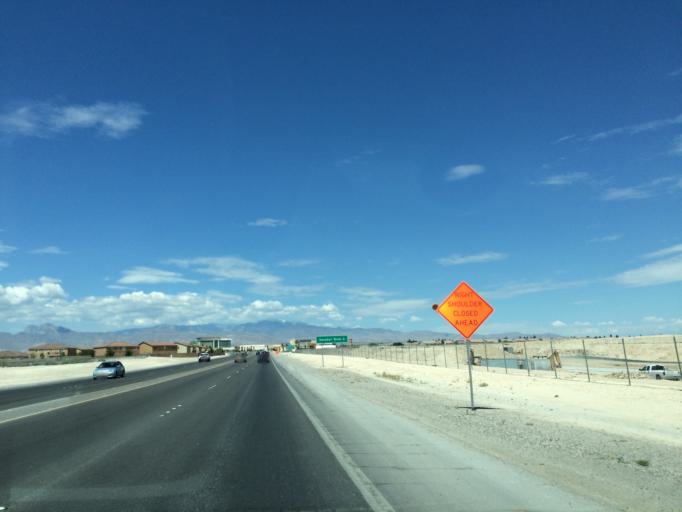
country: US
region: Nevada
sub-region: Clark County
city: North Las Vegas
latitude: 36.2928
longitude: -115.1637
